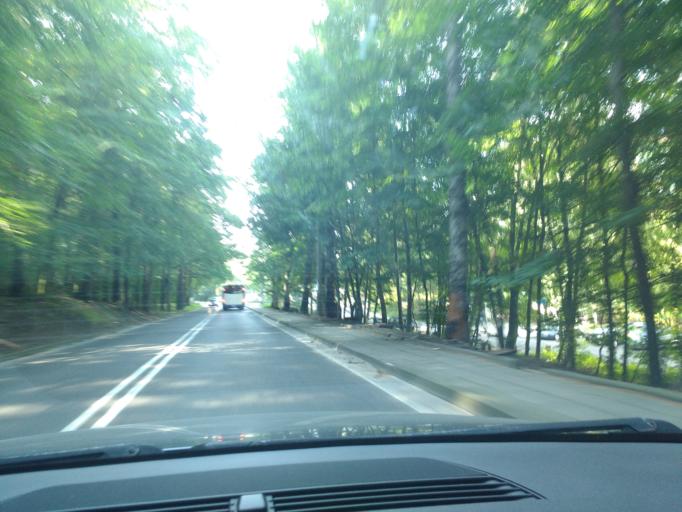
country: PL
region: Pomeranian Voivodeship
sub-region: Sopot
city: Sopot
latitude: 54.4558
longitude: 18.5352
